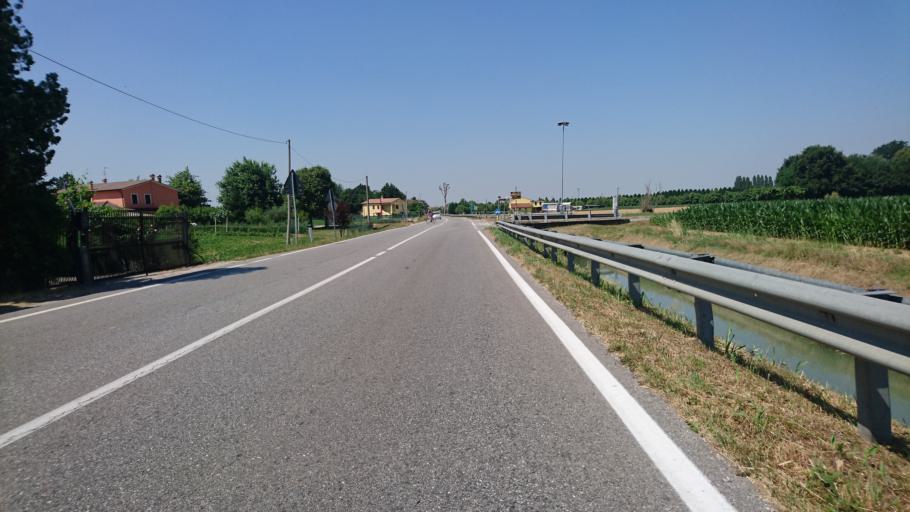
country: IT
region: Veneto
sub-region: Provincia di Padova
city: Bastia
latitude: 45.3929
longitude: 11.6626
